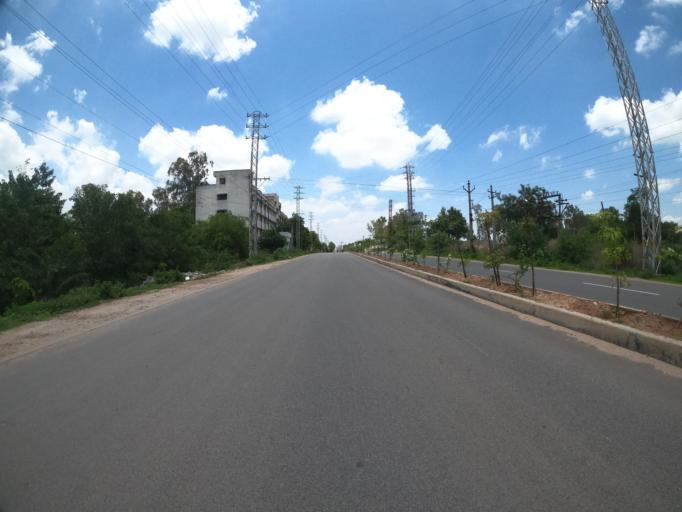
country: IN
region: Telangana
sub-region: Medak
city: Serilingampalle
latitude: 17.3961
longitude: 78.3122
